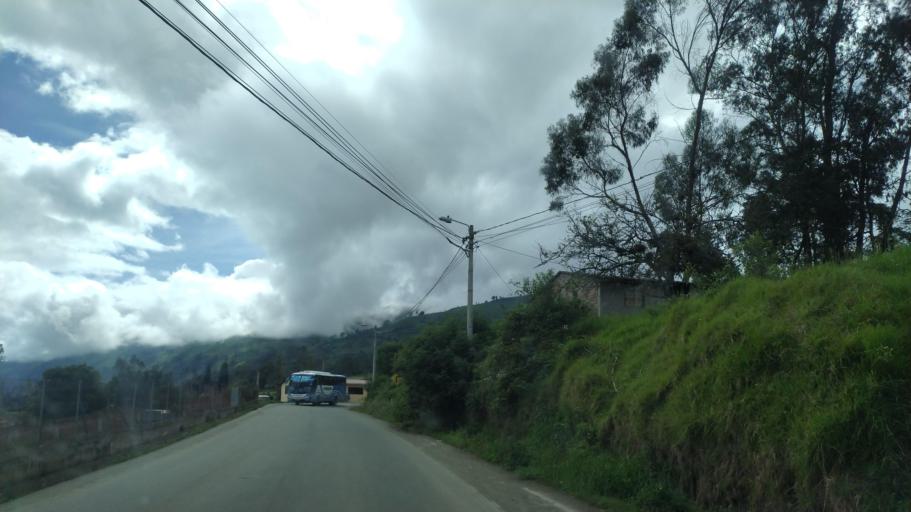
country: EC
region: Chimborazo
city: Riobamba
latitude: -1.6580
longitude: -78.5692
